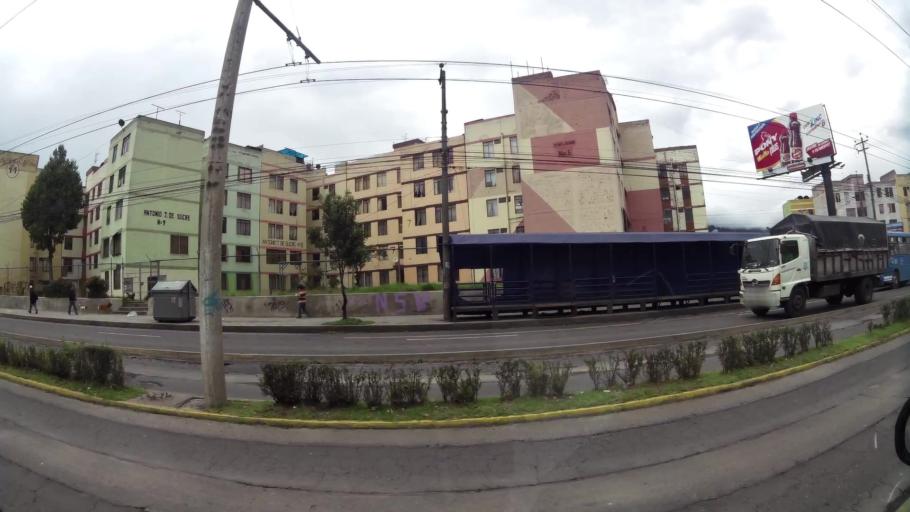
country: EC
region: Pichincha
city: Quito
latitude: -0.2802
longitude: -78.5429
